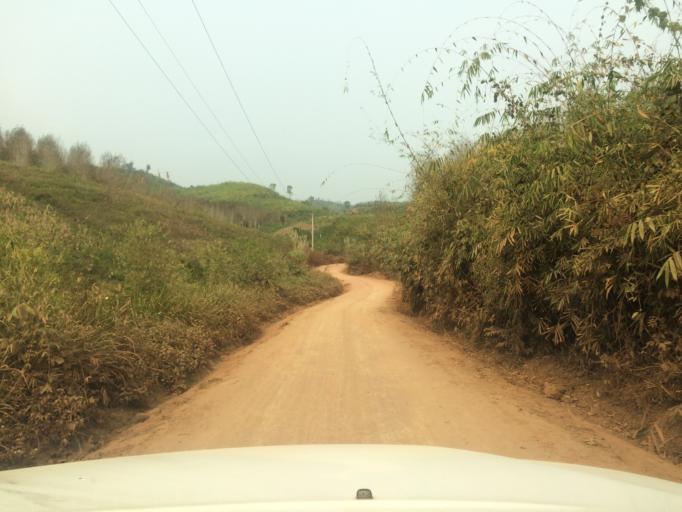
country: LA
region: Loungnamtha
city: Muang Nale
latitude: 20.4178
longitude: 101.6793
